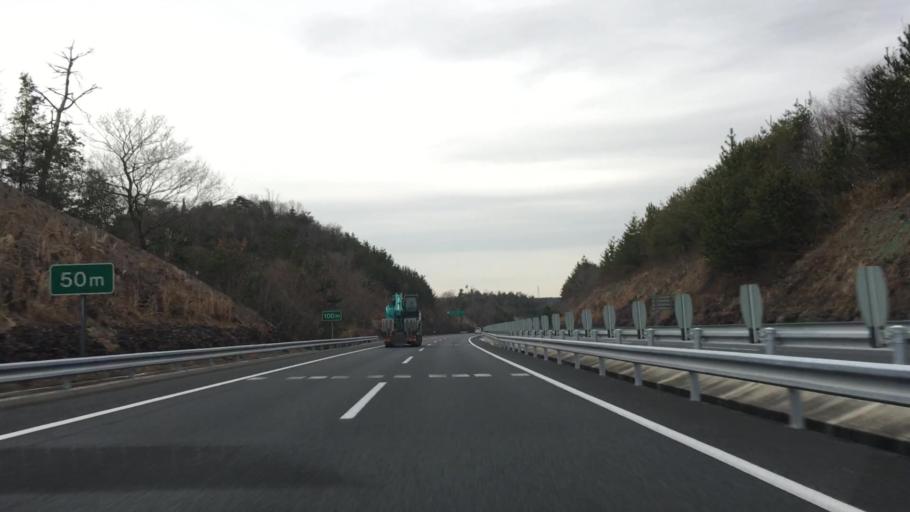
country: JP
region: Gifu
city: Toki
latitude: 35.3109
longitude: 137.1781
